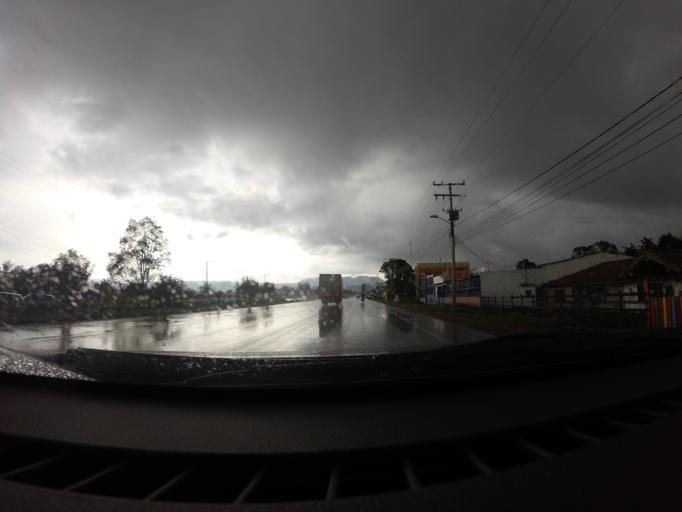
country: CO
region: Cundinamarca
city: El Rosal
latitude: 4.8349
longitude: -74.2511
